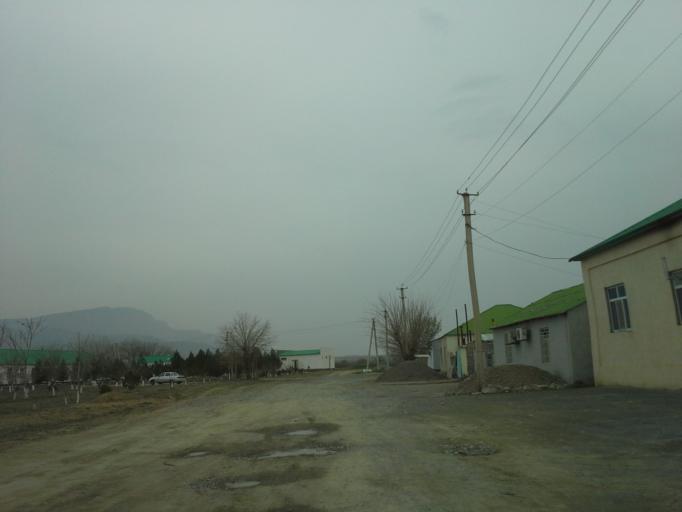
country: TM
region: Ahal
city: Abadan
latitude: 37.9808
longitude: 58.2183
